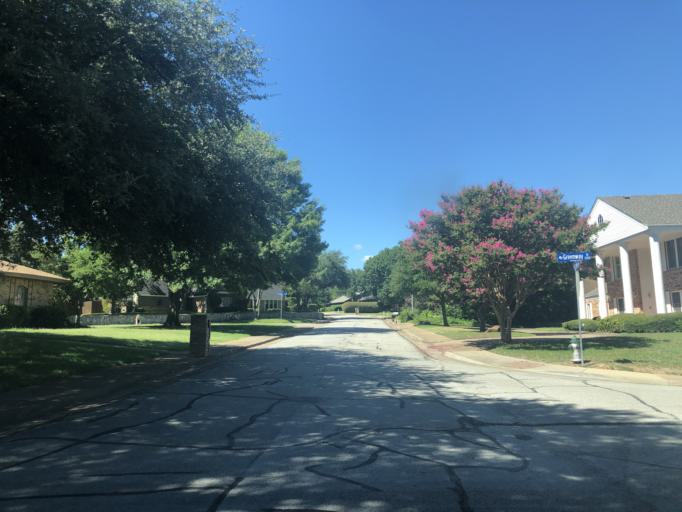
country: US
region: Texas
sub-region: Dallas County
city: Duncanville
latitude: 32.6353
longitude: -96.9284
